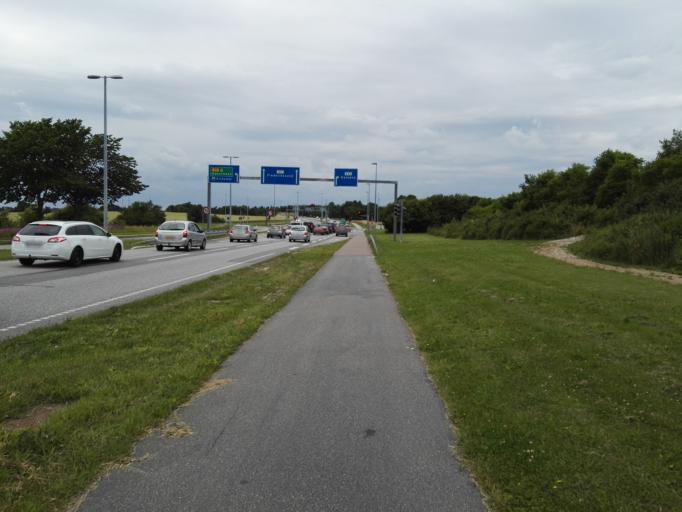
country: DK
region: Capital Region
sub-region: Egedal Kommune
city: Smorumnedre
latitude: 55.7545
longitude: 12.2899
